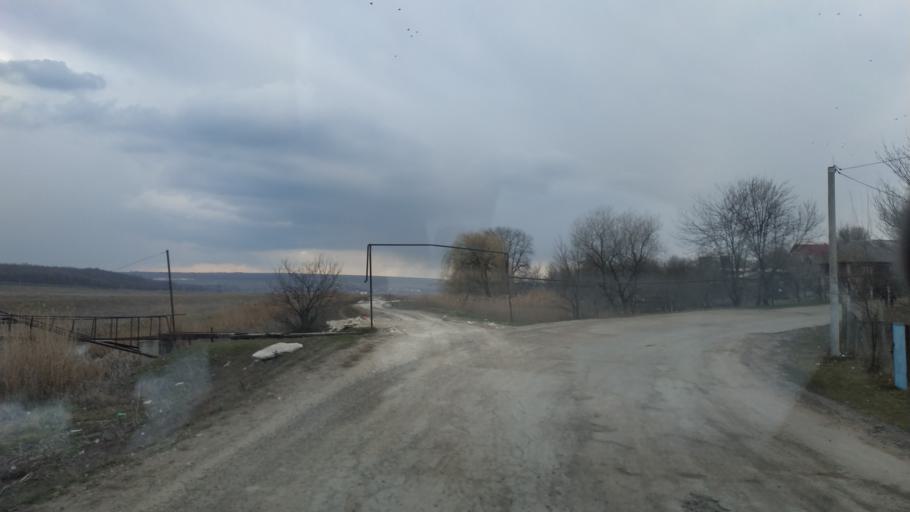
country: MD
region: Anenii Noi
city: Anenii Noi
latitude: 46.8886
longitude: 29.2964
